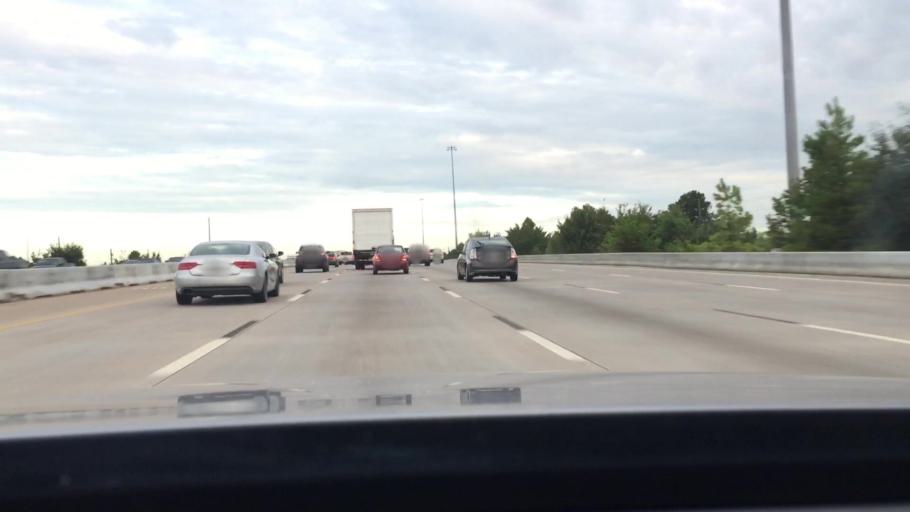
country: US
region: Texas
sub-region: Harris County
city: Jersey Village
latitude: 29.9662
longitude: -95.5549
